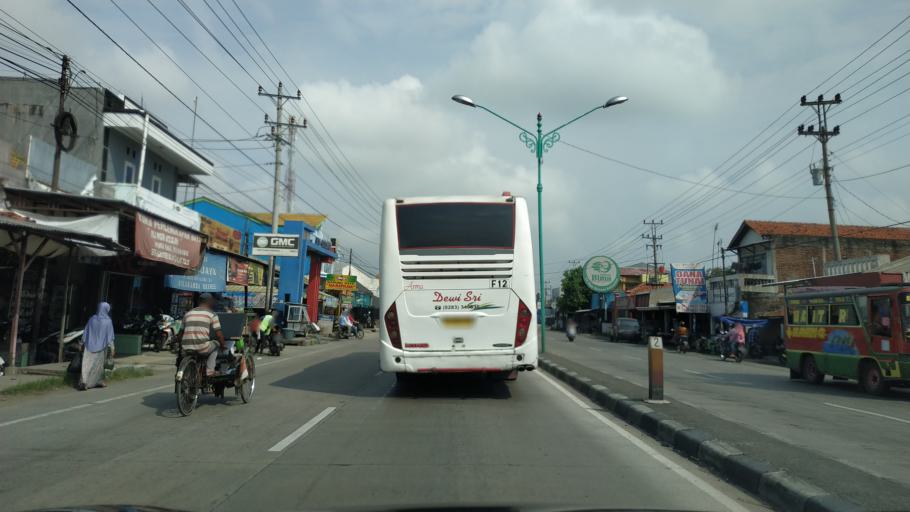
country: ID
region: Central Java
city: Bulakamba
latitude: -6.8739
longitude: 108.9472
